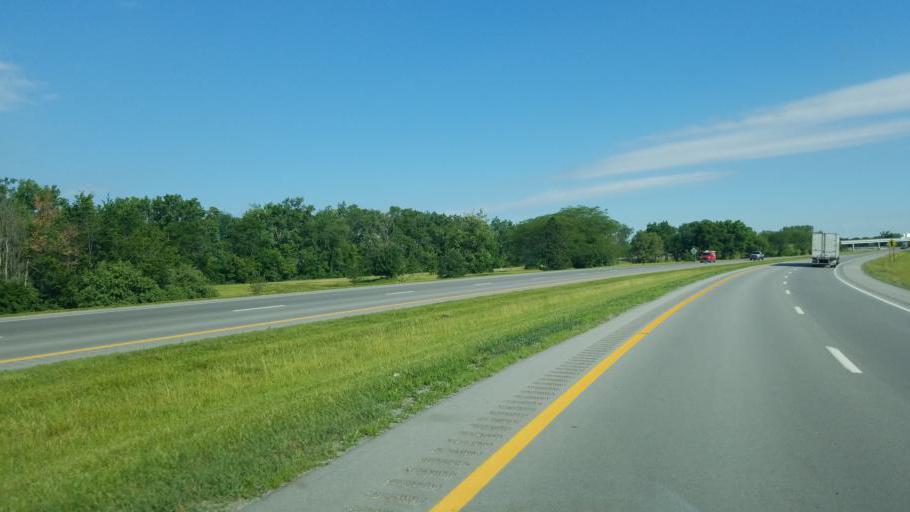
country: US
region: Ohio
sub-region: Hancock County
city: Findlay
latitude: 40.9891
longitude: -83.6490
